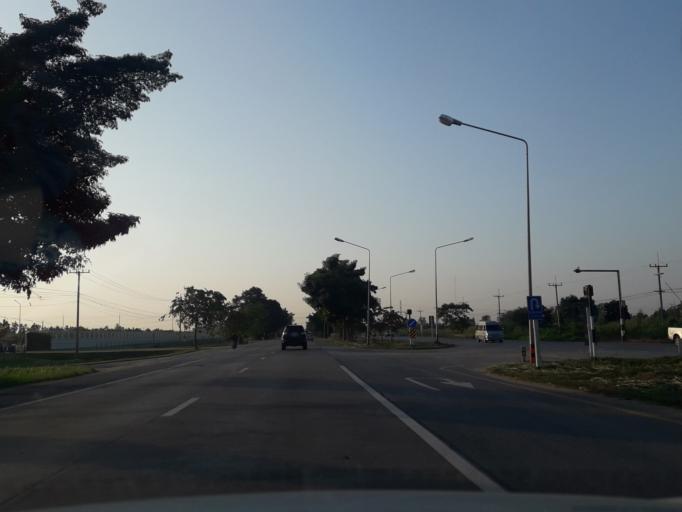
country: TH
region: Phra Nakhon Si Ayutthaya
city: Bang Pa-in
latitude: 14.2838
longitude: 100.5268
